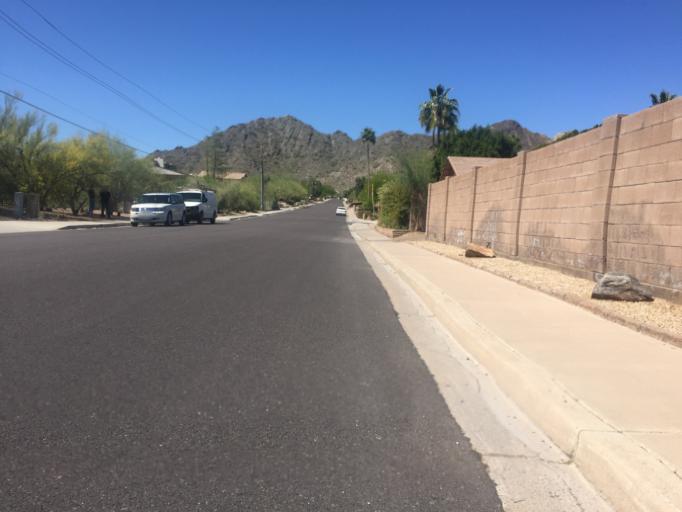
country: US
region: Arizona
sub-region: Maricopa County
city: Paradise Valley
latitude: 33.5749
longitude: -112.0283
